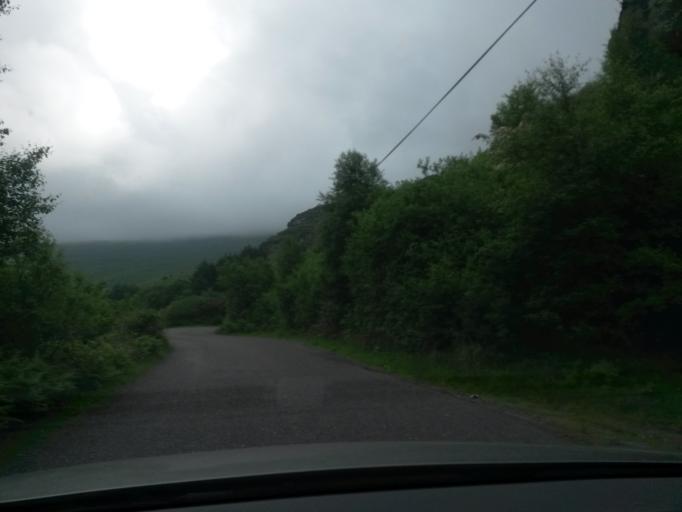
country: IE
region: Munster
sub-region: Ciarrai
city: Killorglin
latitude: 52.0169
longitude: -9.8012
